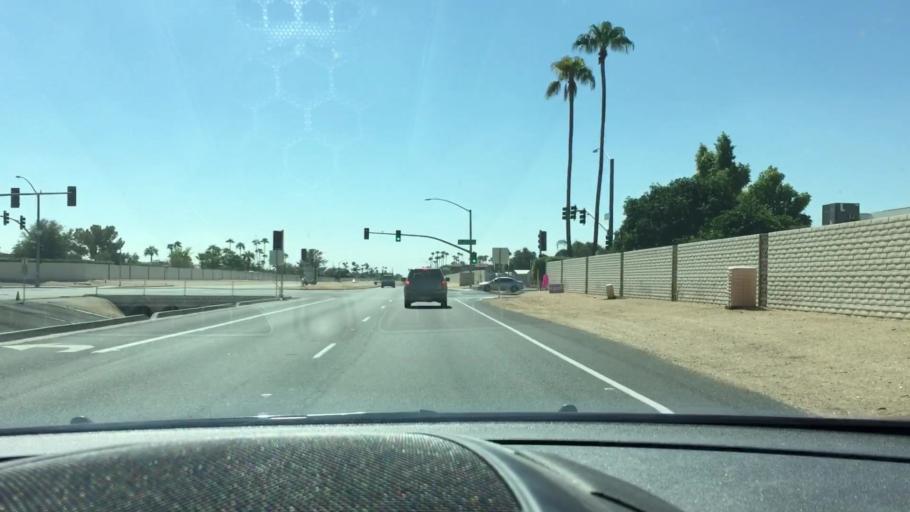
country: US
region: Arizona
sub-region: Maricopa County
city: Sun City
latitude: 33.6471
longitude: -112.2772
